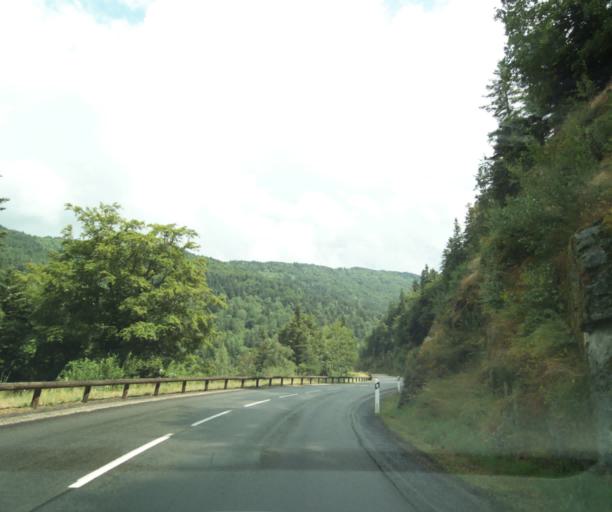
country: FR
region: Auvergne
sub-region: Departement de la Haute-Loire
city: Saugues
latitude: 44.9585
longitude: 3.6267
